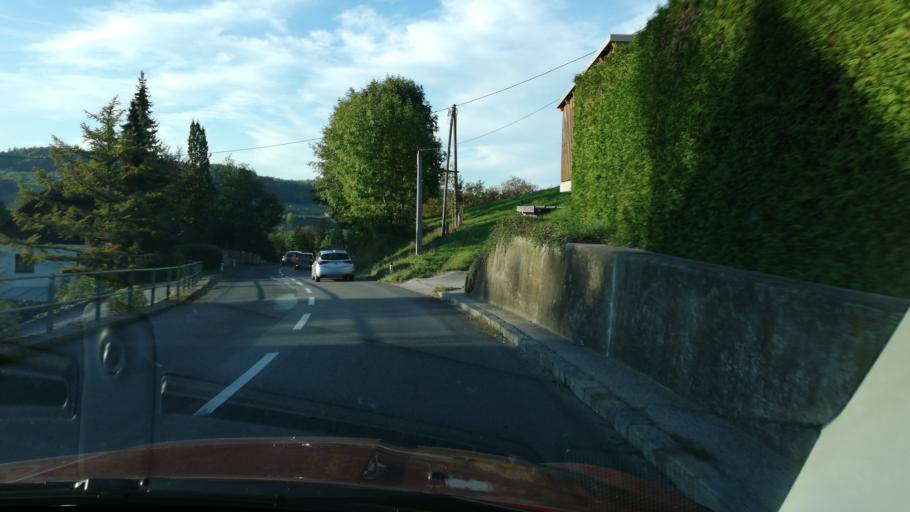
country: AT
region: Upper Austria
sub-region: Politischer Bezirk Kirchdorf an der Krems
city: Gruenburg
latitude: 47.9668
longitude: 14.2751
